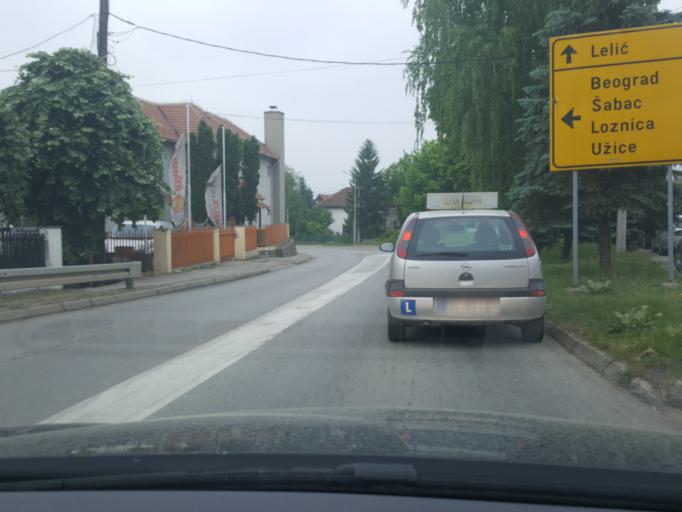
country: RS
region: Central Serbia
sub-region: Kolubarski Okrug
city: Valjevo
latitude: 44.2674
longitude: 19.8790
